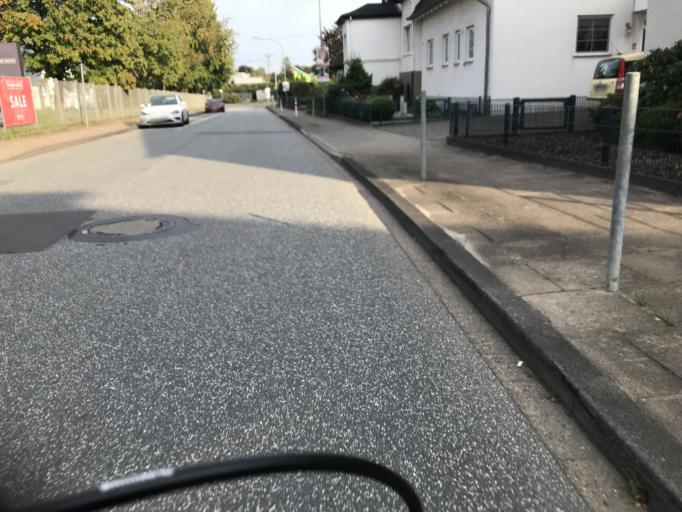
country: DE
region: North Rhine-Westphalia
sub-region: Regierungsbezirk Detmold
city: Herford
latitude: 52.1137
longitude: 8.6554
